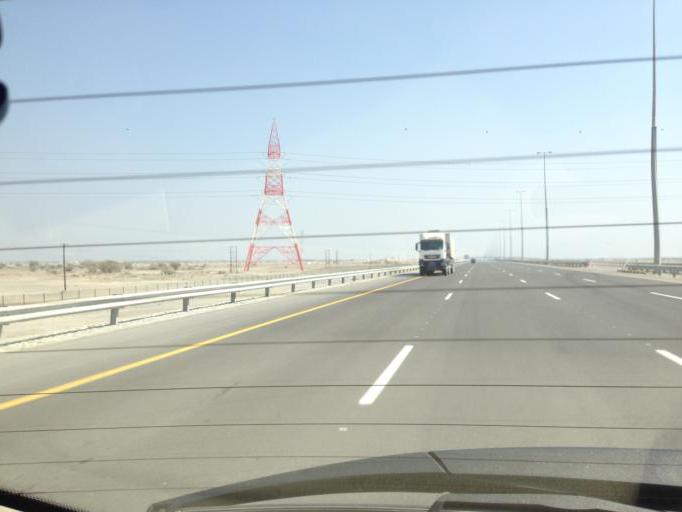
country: OM
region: Al Batinah
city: Barka'
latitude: 23.6108
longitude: 57.8291
